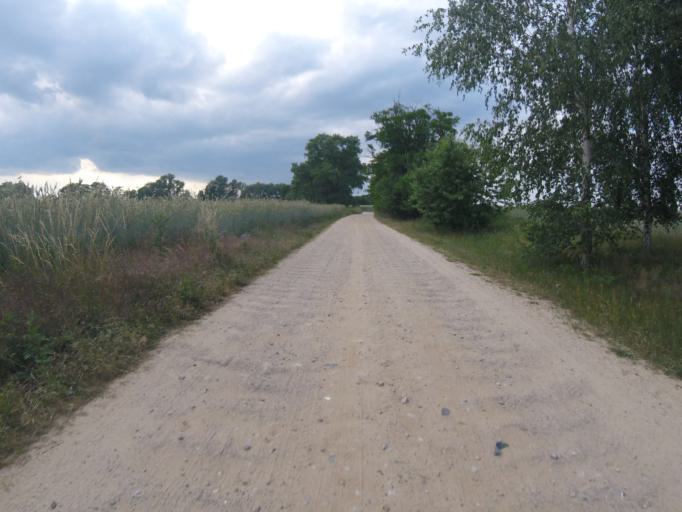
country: DE
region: Brandenburg
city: Bestensee
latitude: 52.2538
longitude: 13.6236
